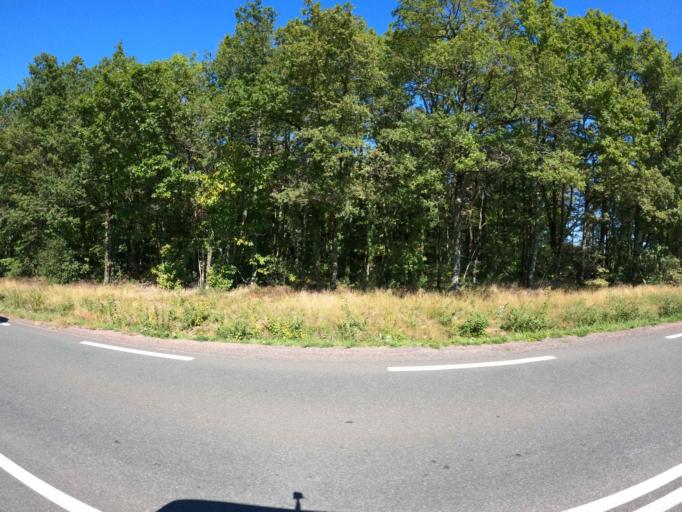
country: FR
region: Limousin
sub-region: Departement de la Haute-Vienne
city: Chateauponsac
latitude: 46.1916
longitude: 1.2521
